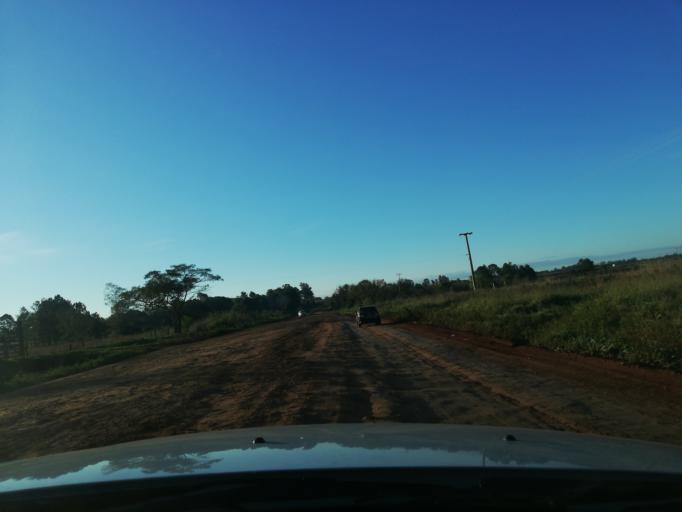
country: AR
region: Misiones
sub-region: Departamento de Capital
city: Posadas
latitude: -27.4706
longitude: -55.9708
